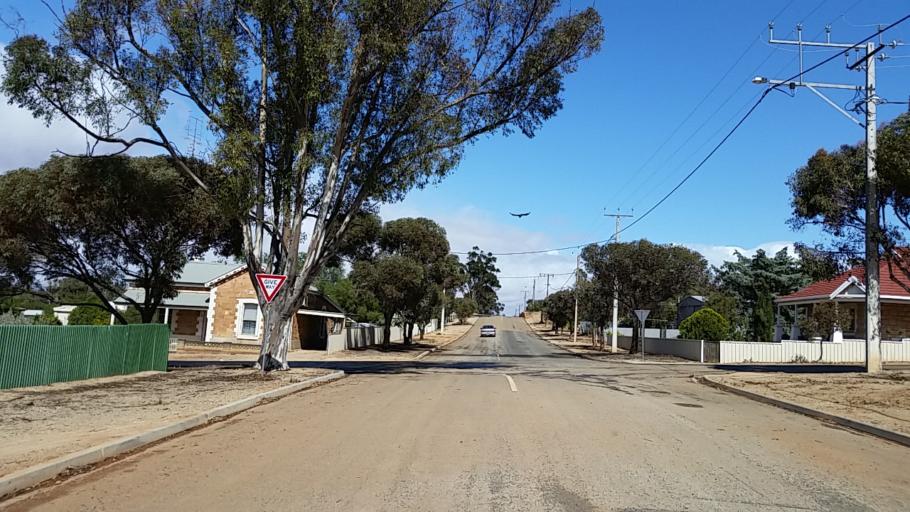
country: AU
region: South Australia
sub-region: Peterborough
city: Peterborough
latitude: -32.9701
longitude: 138.8364
